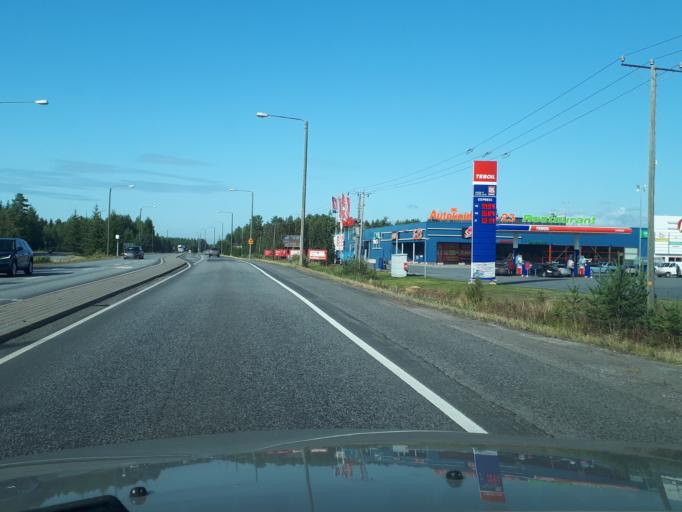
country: FI
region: Northern Ostrobothnia
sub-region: Oulunkaari
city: Ii
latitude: 65.2895
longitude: 25.3731
